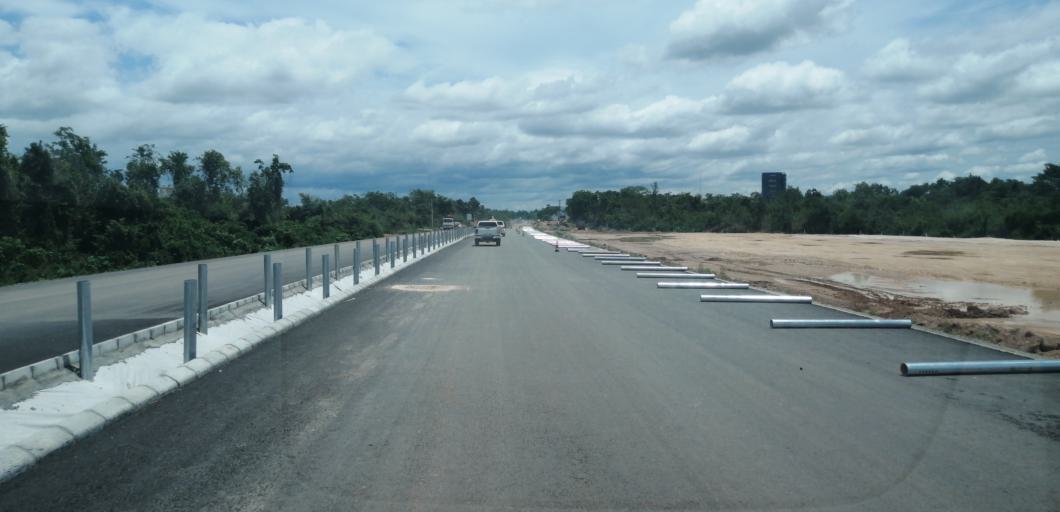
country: LA
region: Vientiane
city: Muang Phon-Hong
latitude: 18.2934
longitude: 102.4579
